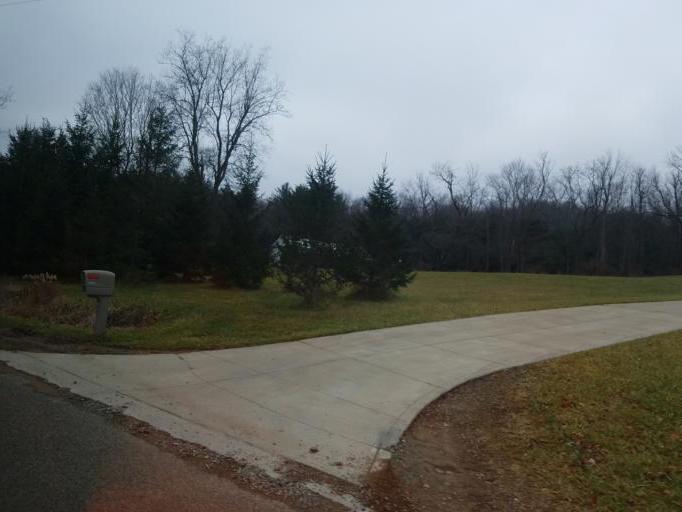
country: US
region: Ohio
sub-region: Richland County
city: Lexington
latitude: 40.6713
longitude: -82.5345
